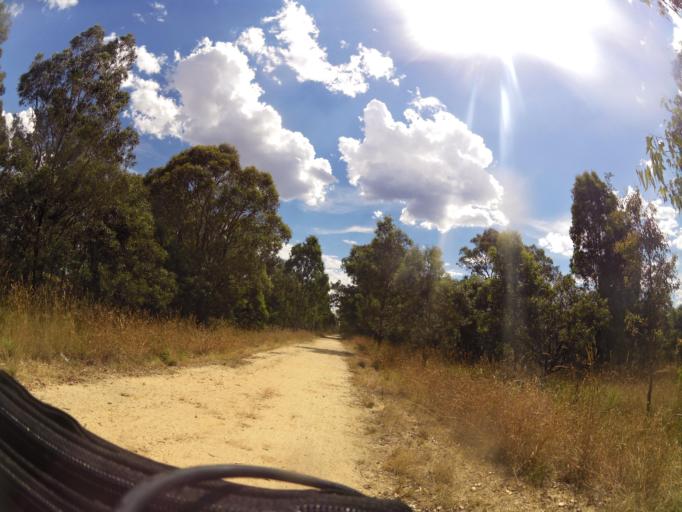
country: AU
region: Victoria
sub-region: Wellington
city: Heyfield
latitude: -37.9823
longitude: 146.7309
